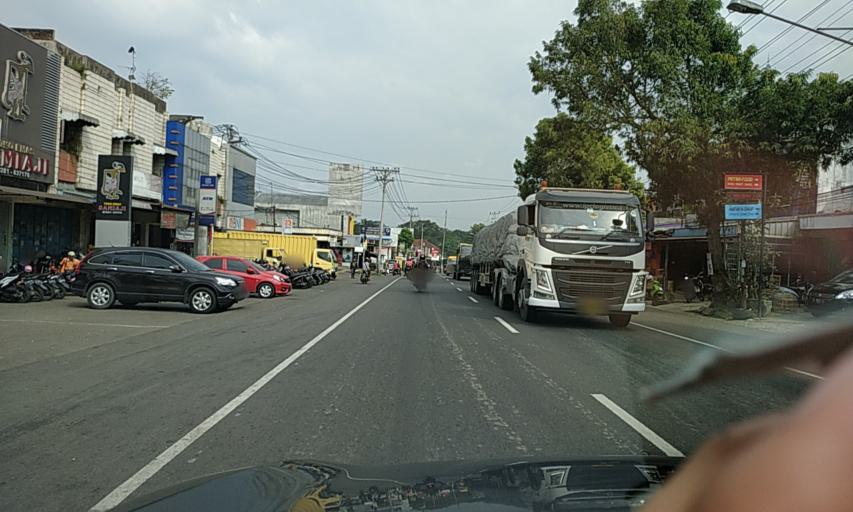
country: ID
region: Central Java
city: Purwokerto
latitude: -7.4203
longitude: 109.1989
